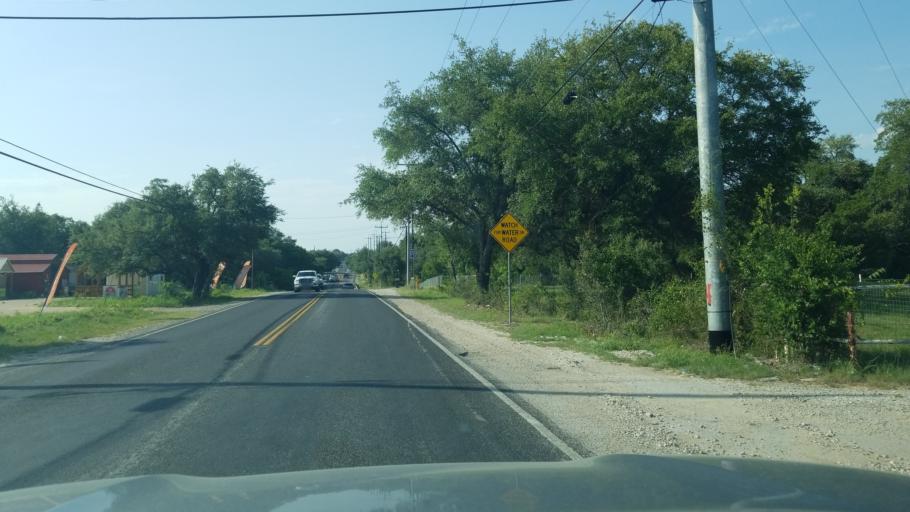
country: US
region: Texas
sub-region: Bexar County
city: Leon Valley
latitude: 29.4441
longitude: -98.7514
